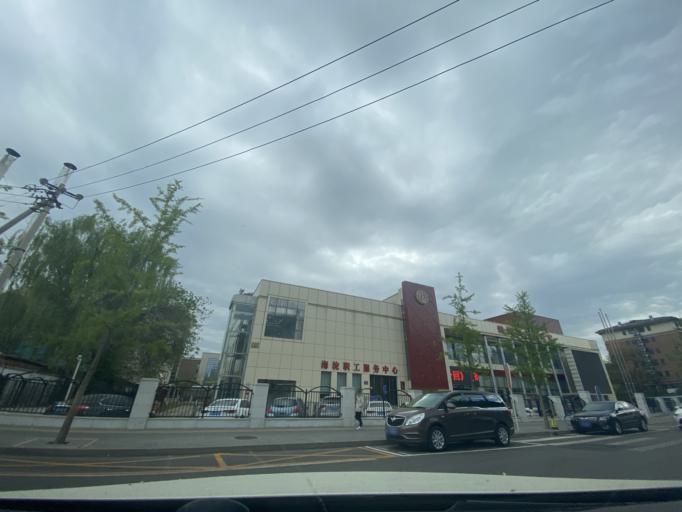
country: CN
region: Beijing
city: Haidian
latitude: 39.9707
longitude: 116.2895
